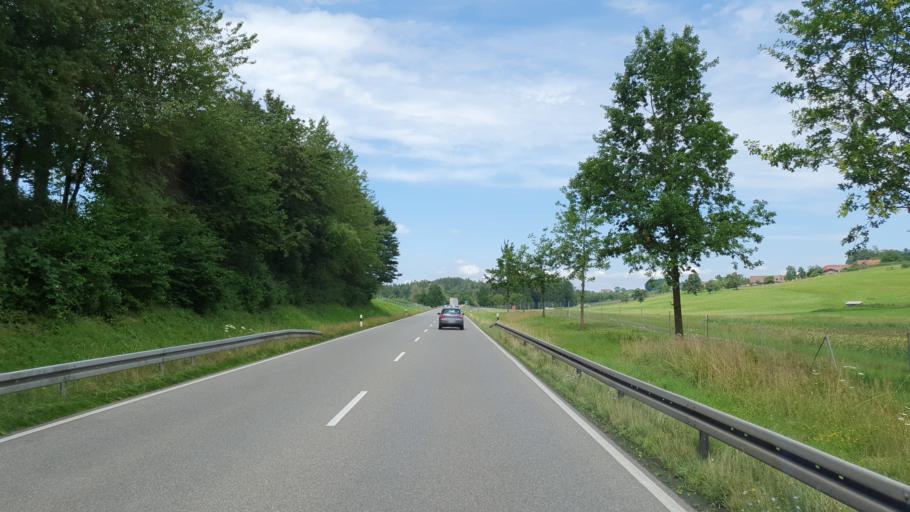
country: DE
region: Bavaria
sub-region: Swabia
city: Bodolz
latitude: 47.5864
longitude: 9.6576
